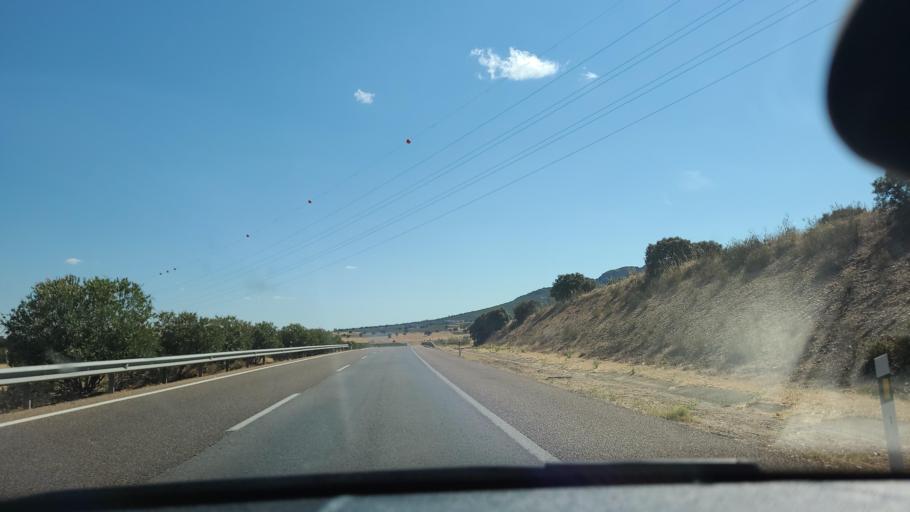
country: ES
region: Extremadura
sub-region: Provincia de Badajoz
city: Calamonte
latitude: 38.8466
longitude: -6.3622
